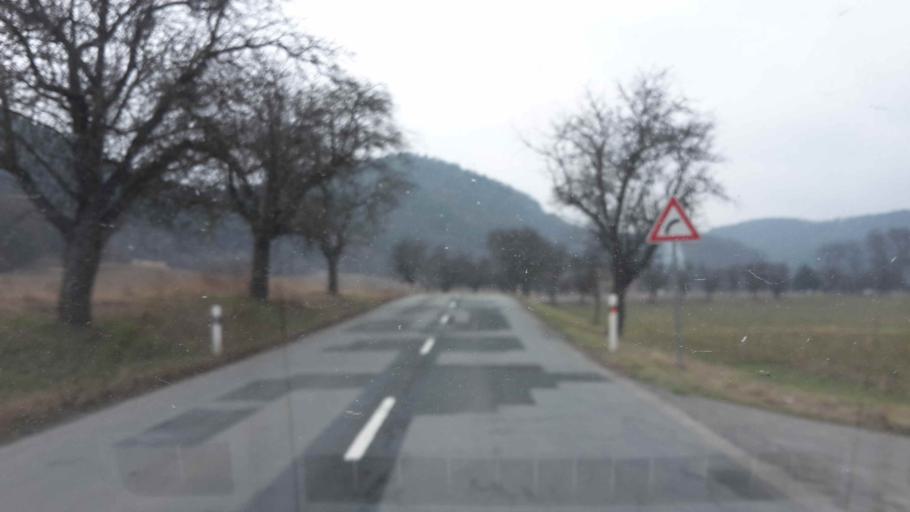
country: CZ
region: South Moravian
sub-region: Okres Brno-Venkov
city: Dolni Loucky
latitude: 49.3916
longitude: 16.3701
